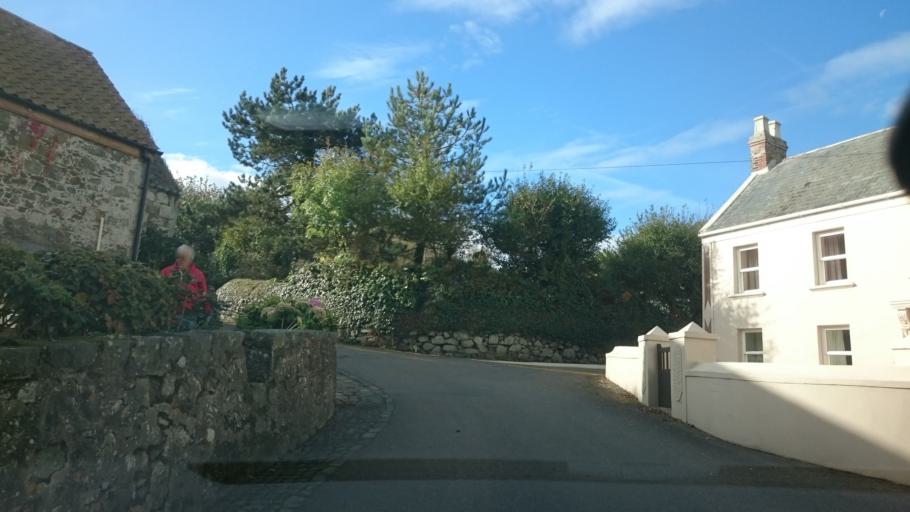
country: GG
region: St Peter Port
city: Saint Peter Port
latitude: 49.4302
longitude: -2.6645
